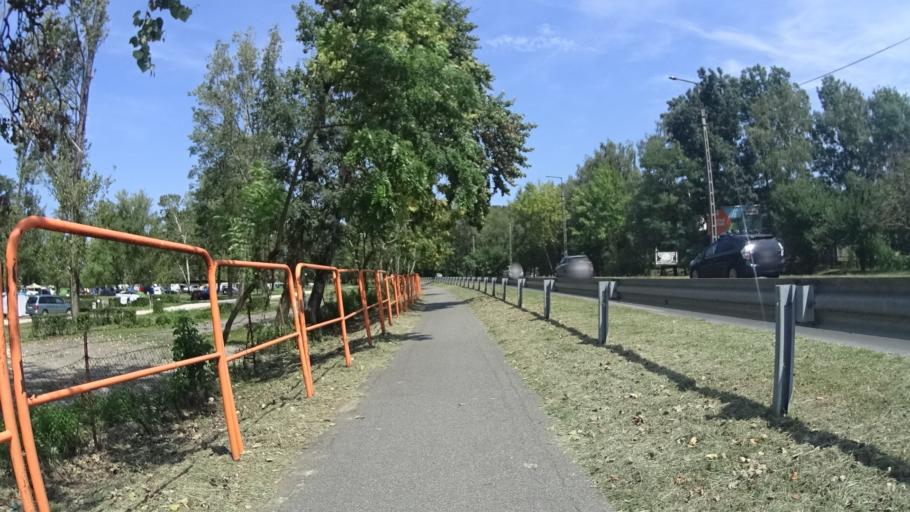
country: HU
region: Somogy
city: Balatonfenyves
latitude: 46.7334
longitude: 17.5338
